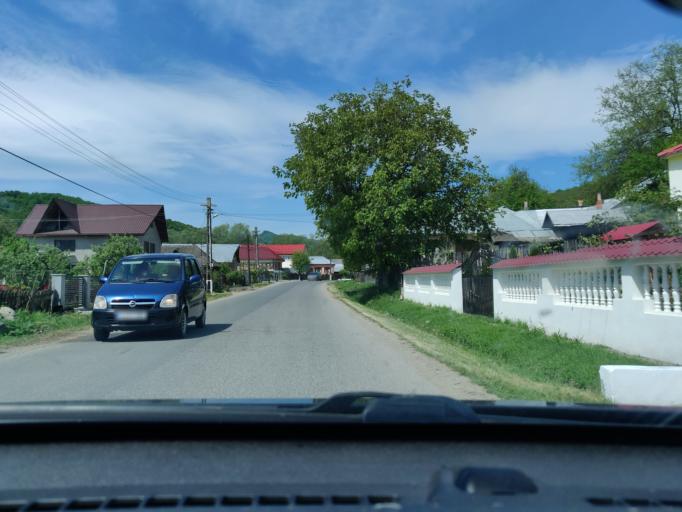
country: RO
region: Vrancea
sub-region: Comuna Racoasa
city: Racoasa
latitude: 45.9550
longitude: 26.8435
